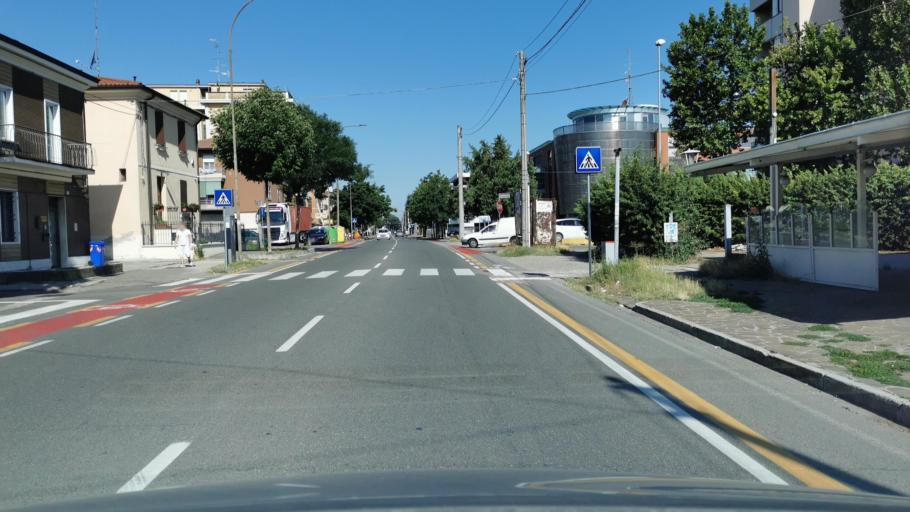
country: IT
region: Emilia-Romagna
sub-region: Provincia di Modena
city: Carpi Centro
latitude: 44.7885
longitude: 10.8886
